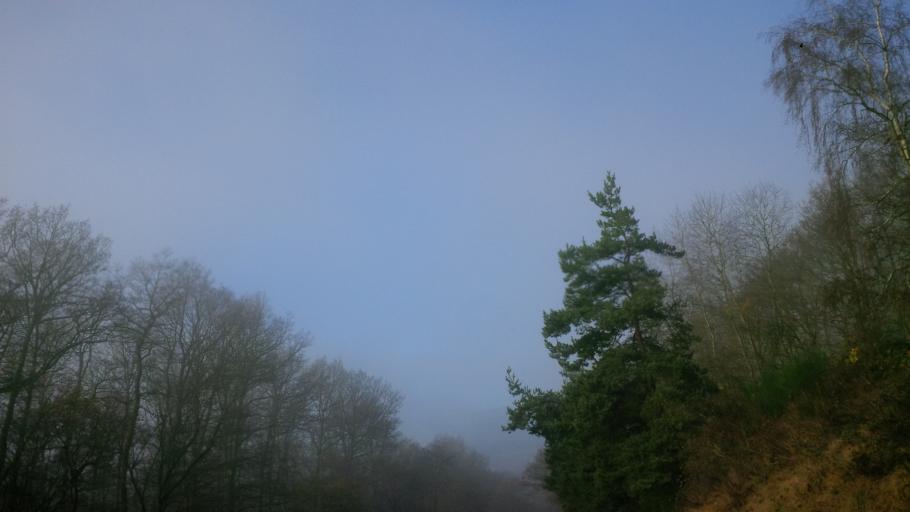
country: DE
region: Hesse
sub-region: Regierungsbezirk Darmstadt
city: Schmitten
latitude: 50.2828
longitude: 8.4719
